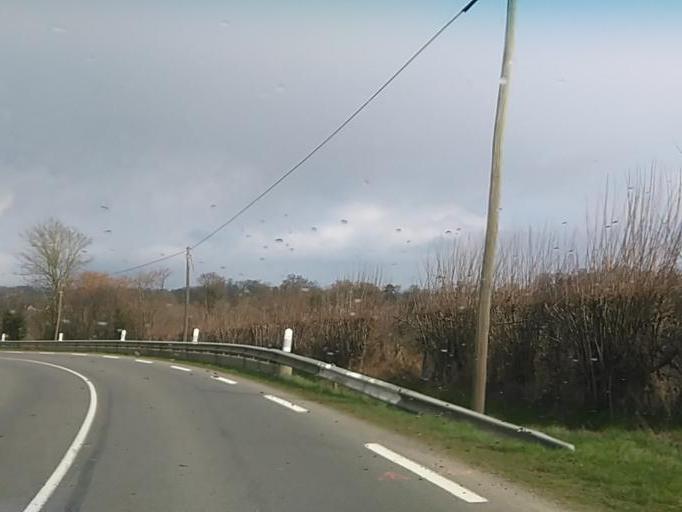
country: FR
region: Lower Normandy
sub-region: Departement de l'Orne
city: Pont-Ecrepin
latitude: 48.7538
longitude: -0.2402
